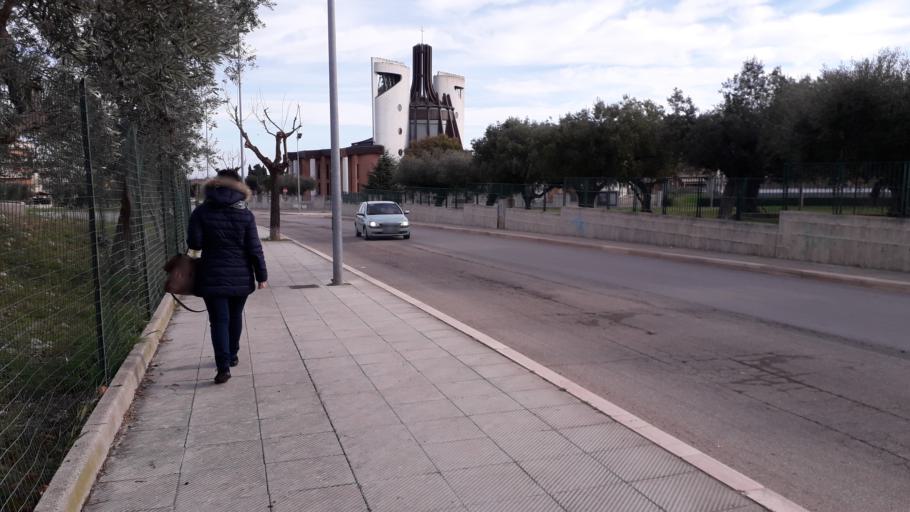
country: IT
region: Molise
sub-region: Provincia di Campobasso
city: Campomarino
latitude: 41.9508
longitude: 15.0327
